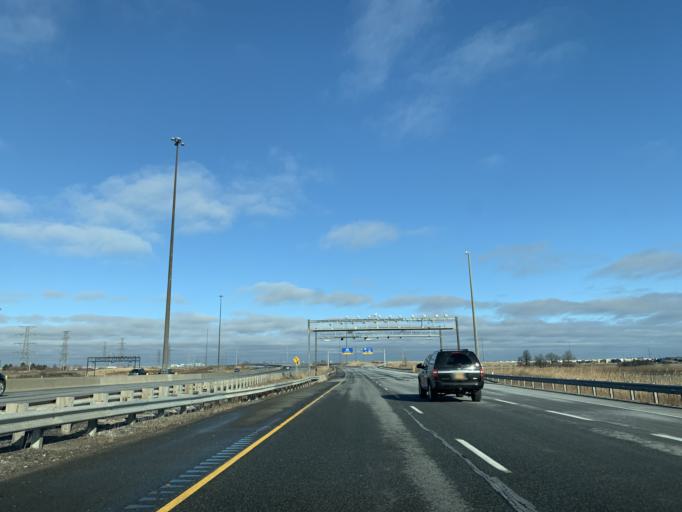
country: CA
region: Ontario
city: Oakville
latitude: 43.5205
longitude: -79.7337
